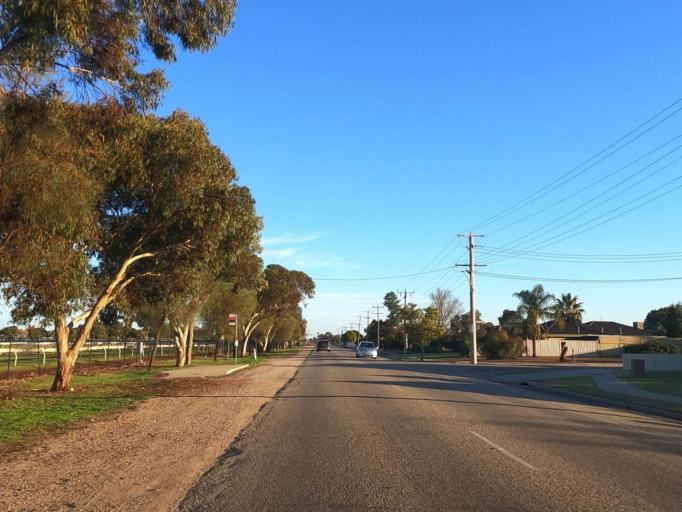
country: AU
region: Victoria
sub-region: Swan Hill
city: Swan Hill
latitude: -35.3505
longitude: 143.5543
